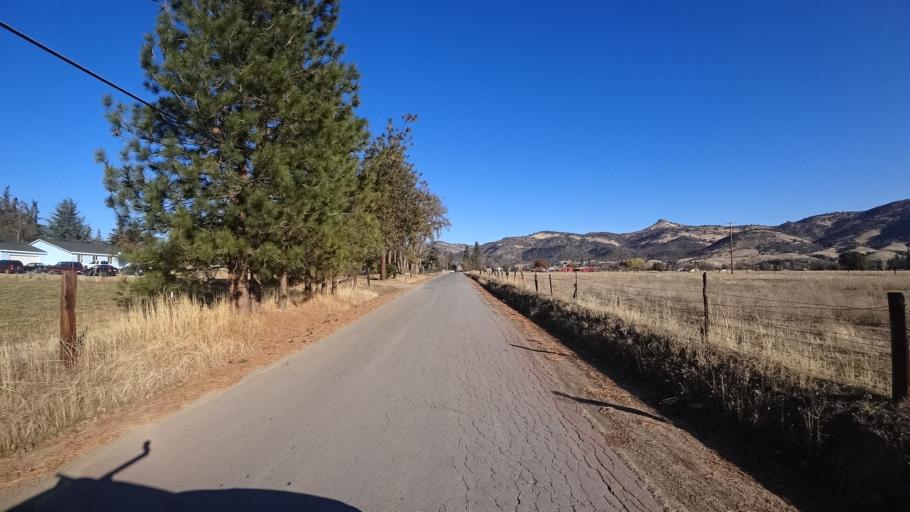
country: US
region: California
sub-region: Siskiyou County
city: Montague
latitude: 41.9053
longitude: -122.5631
